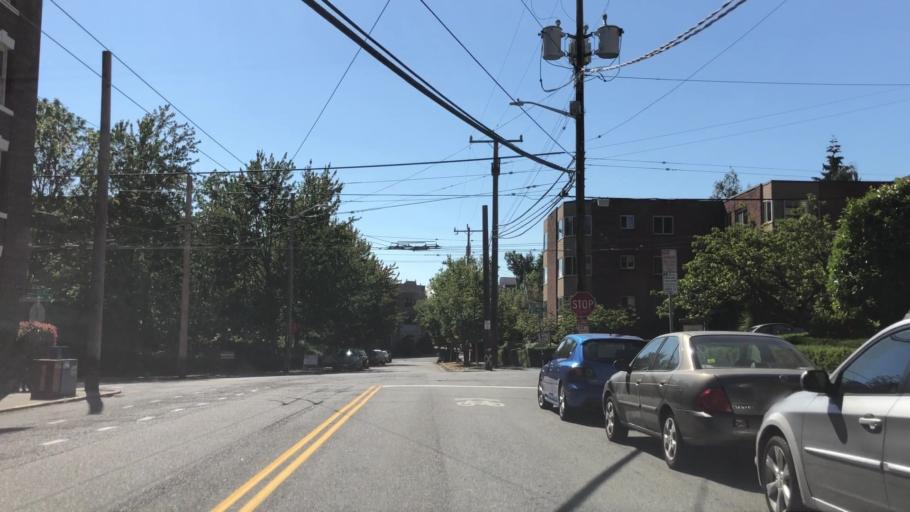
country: US
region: Washington
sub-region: King County
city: Seattle
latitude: 47.6258
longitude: -122.3588
